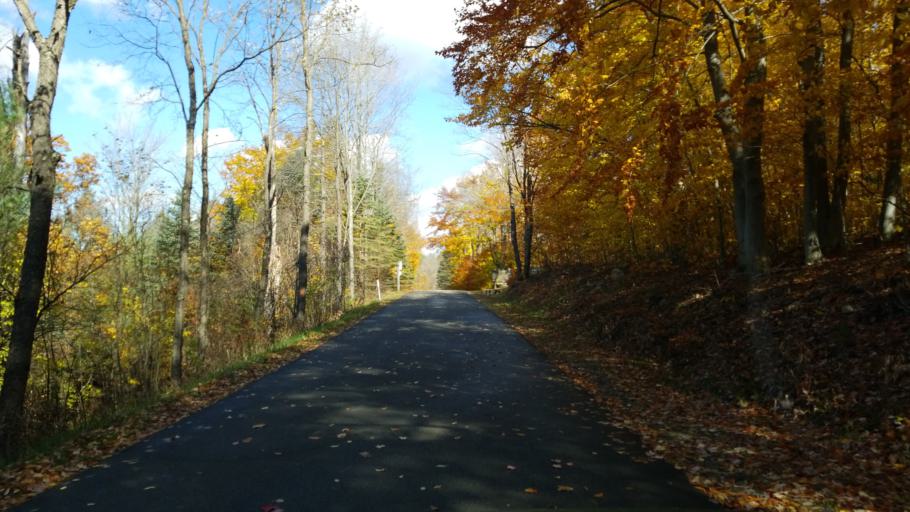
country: US
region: Pennsylvania
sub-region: Clearfield County
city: Clearfield
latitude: 41.1957
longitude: -78.5064
